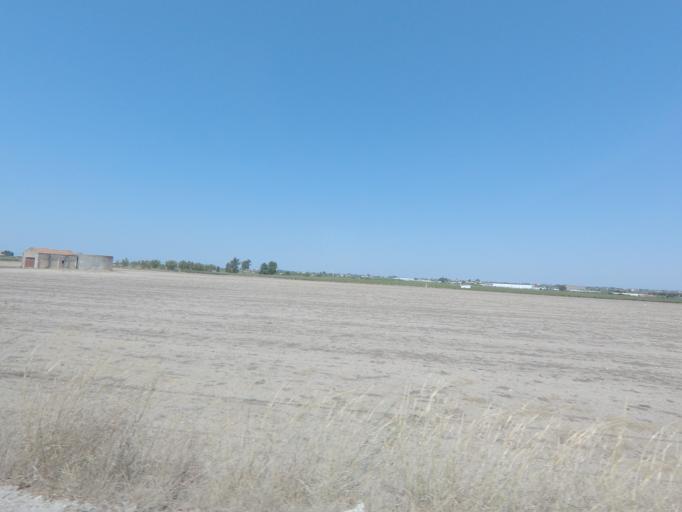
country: PT
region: Setubal
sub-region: Palmela
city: Palmela
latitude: 38.5912
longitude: -8.8536
